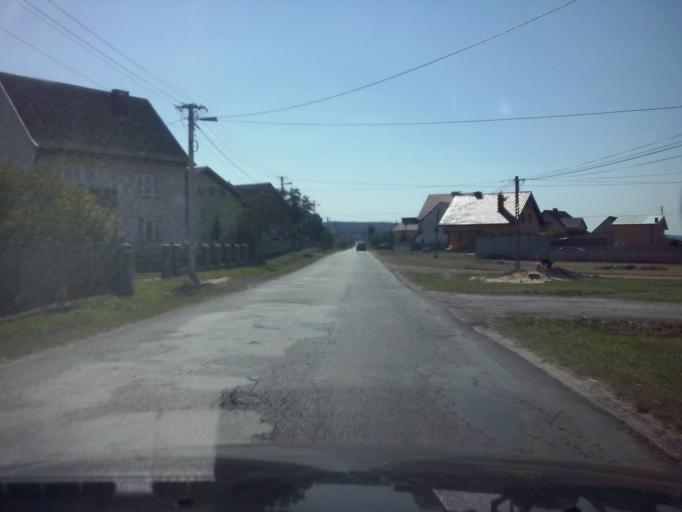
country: PL
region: Swietokrzyskie
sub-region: Powiat kielecki
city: Gorno
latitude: 50.8500
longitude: 20.8117
